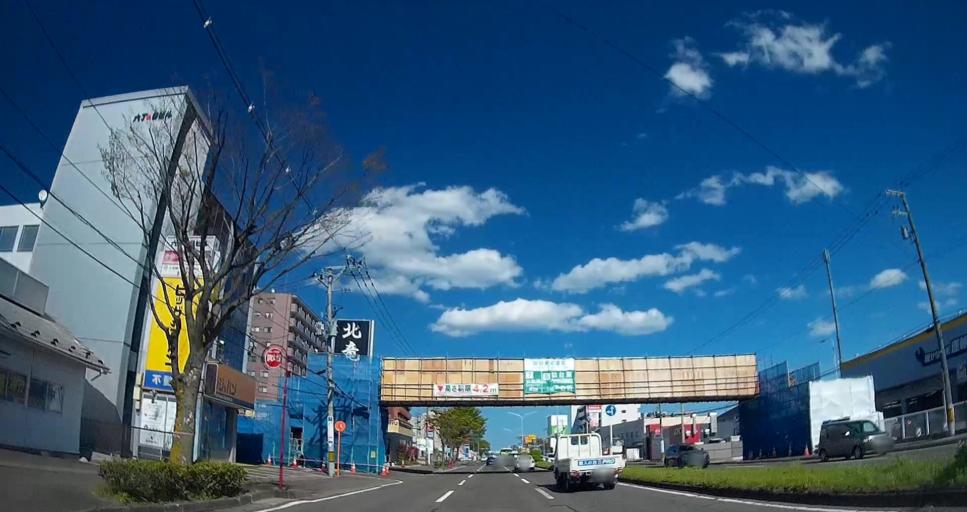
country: JP
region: Miyagi
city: Sendai-shi
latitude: 38.2509
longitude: 140.9385
